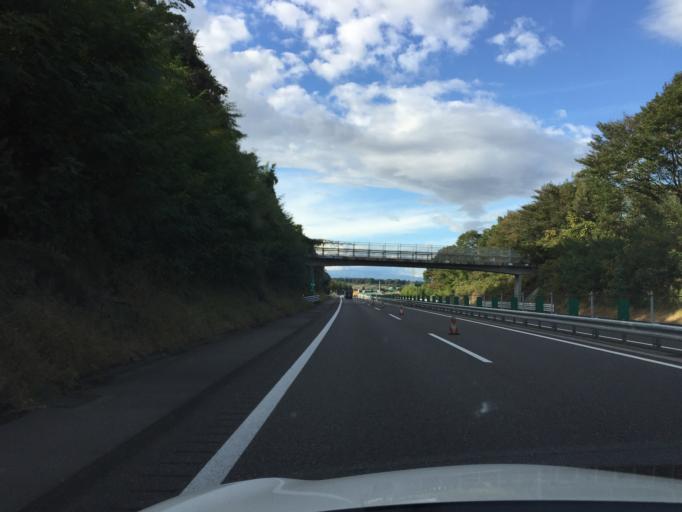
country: JP
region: Fukushima
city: Sukagawa
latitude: 37.3225
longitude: 140.3412
